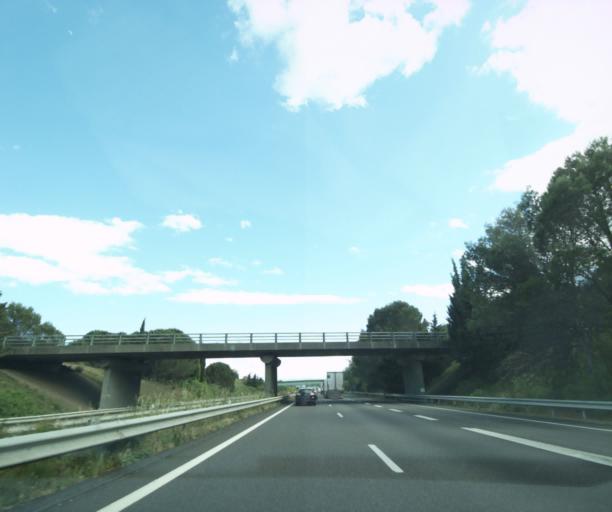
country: FR
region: Languedoc-Roussillon
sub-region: Departement du Gard
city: Garons
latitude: 43.7587
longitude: 4.4267
